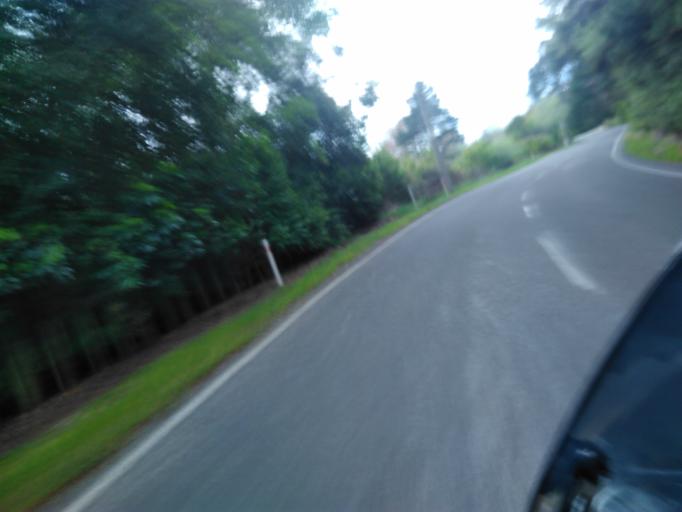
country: NZ
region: Gisborne
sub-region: Gisborne District
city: Gisborne
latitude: -38.6756
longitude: 177.8084
